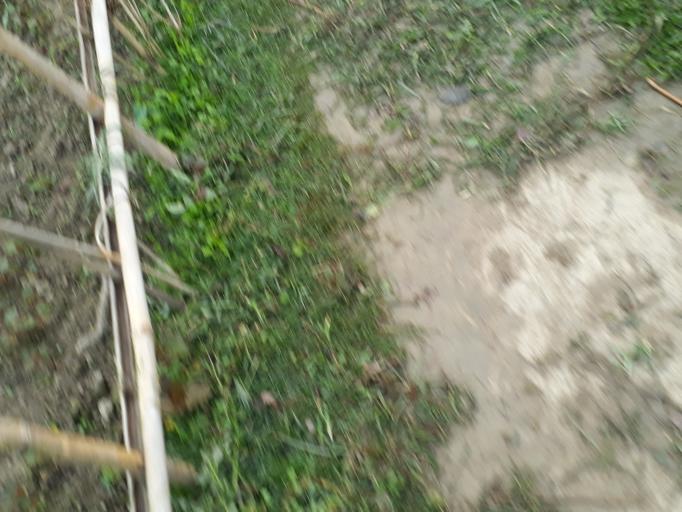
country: BD
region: Rajshahi
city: Sirajganj
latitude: 24.3233
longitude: 89.6734
